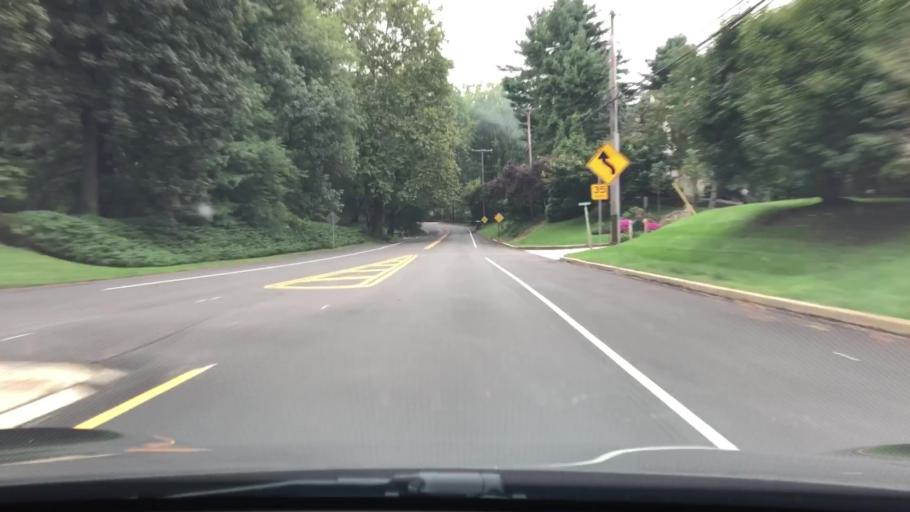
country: US
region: Pennsylvania
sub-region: Delaware County
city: Broomall
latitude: 39.9983
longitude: -75.3591
